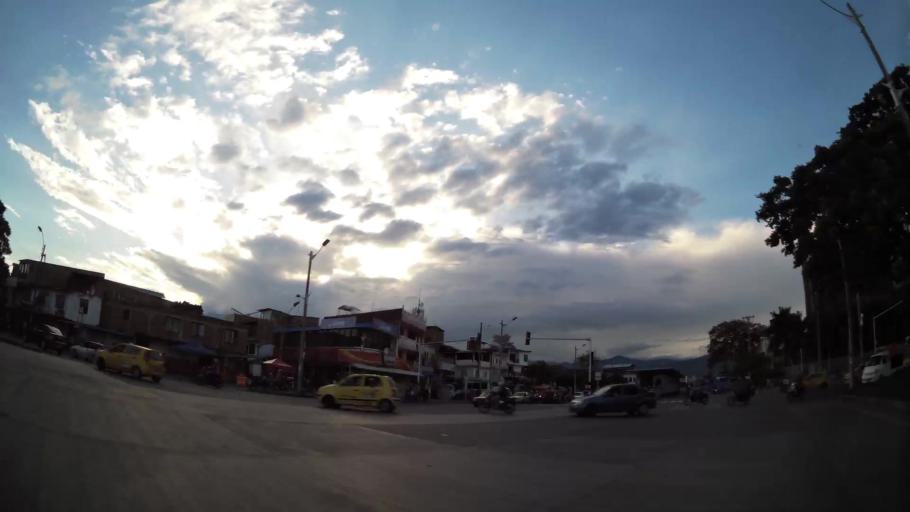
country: CO
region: Valle del Cauca
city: Cali
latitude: 3.4183
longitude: -76.4862
